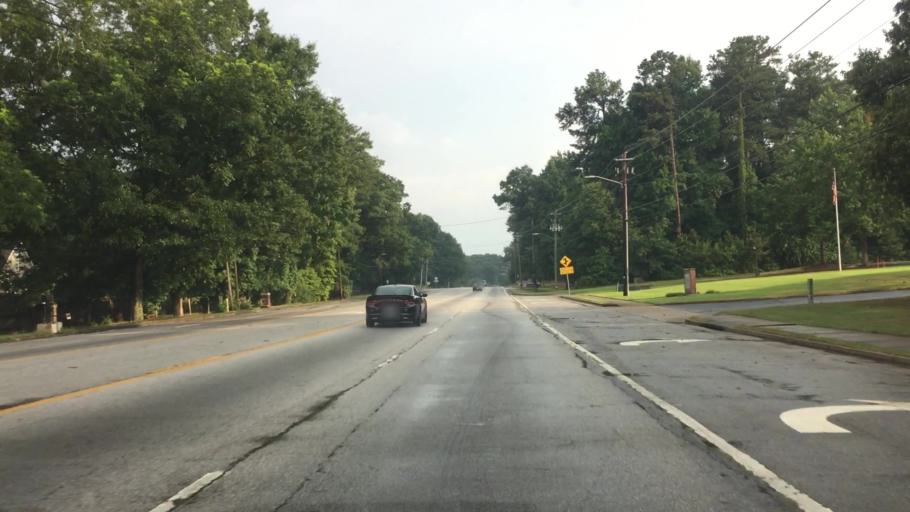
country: US
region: Georgia
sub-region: DeKalb County
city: Candler-McAfee
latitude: 33.7287
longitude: -84.2141
